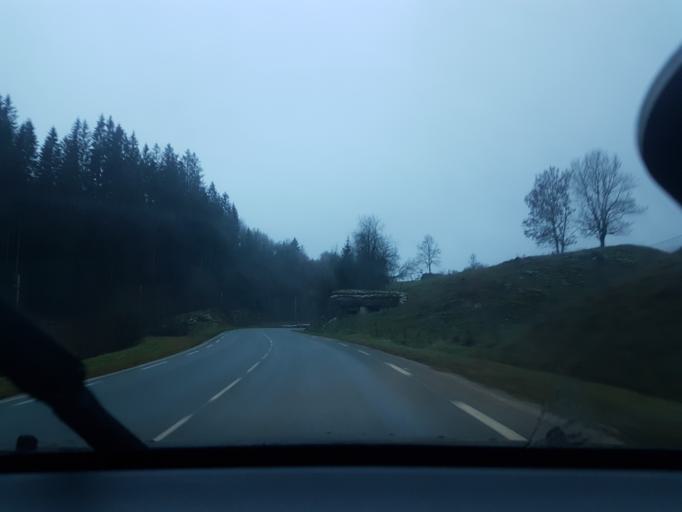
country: FR
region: Franche-Comte
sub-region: Departement du Doubs
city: La Cluse-et-Mijoux
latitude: 46.8887
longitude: 6.4335
